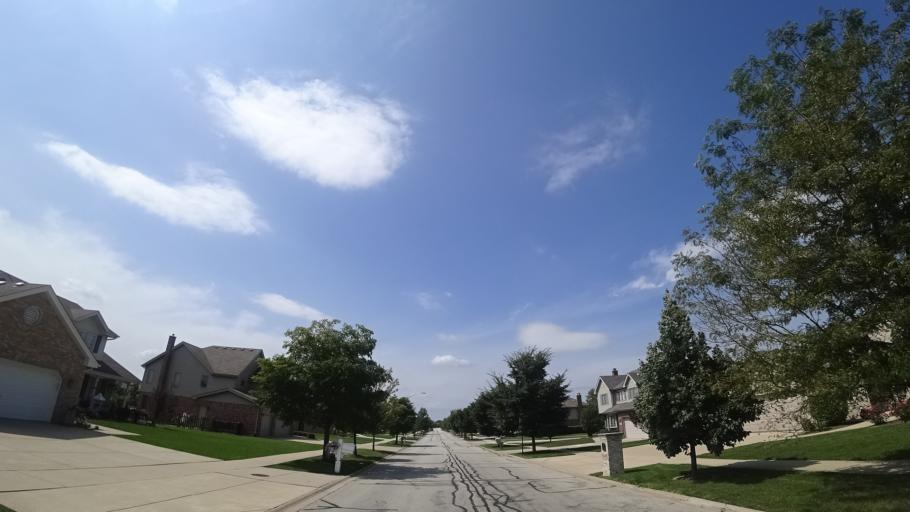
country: US
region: Illinois
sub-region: Cook County
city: Orland Hills
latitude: 41.5680
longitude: -87.8225
